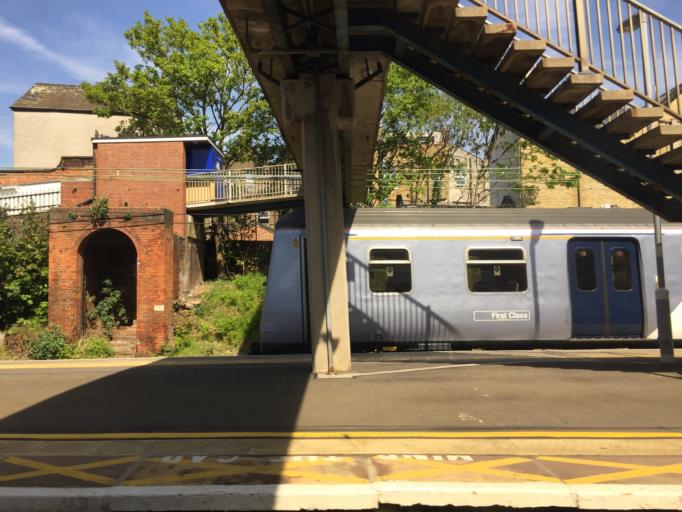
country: GB
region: England
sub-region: Greater London
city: Ilford
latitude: 51.5587
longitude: 0.0678
